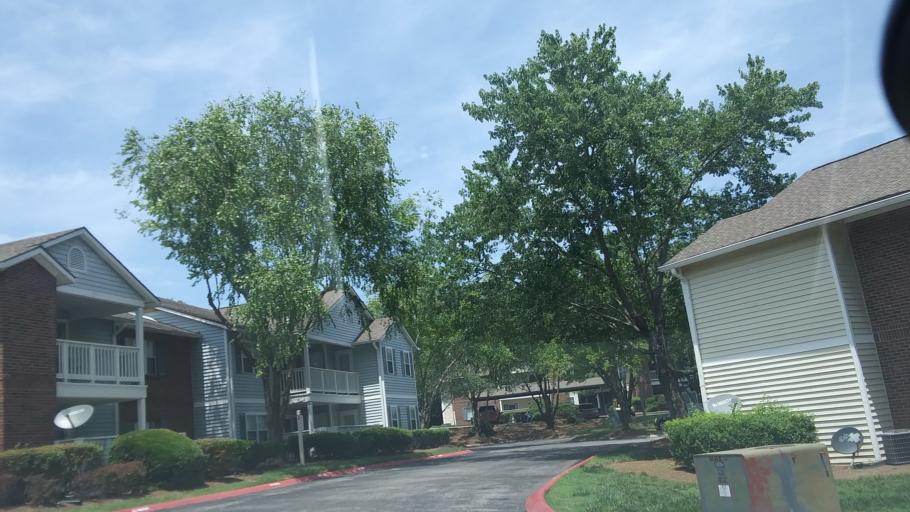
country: US
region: Tennessee
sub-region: Rutherford County
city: La Vergne
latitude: 36.0901
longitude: -86.6422
